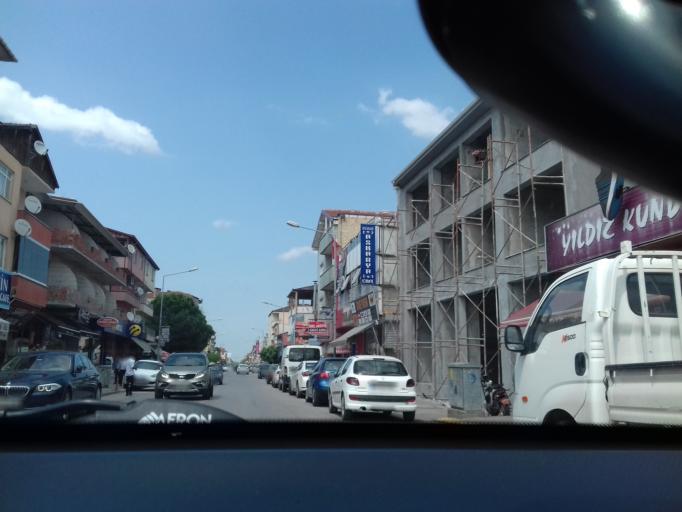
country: TR
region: Sakarya
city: Adapazari
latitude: 40.7144
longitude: 30.3627
